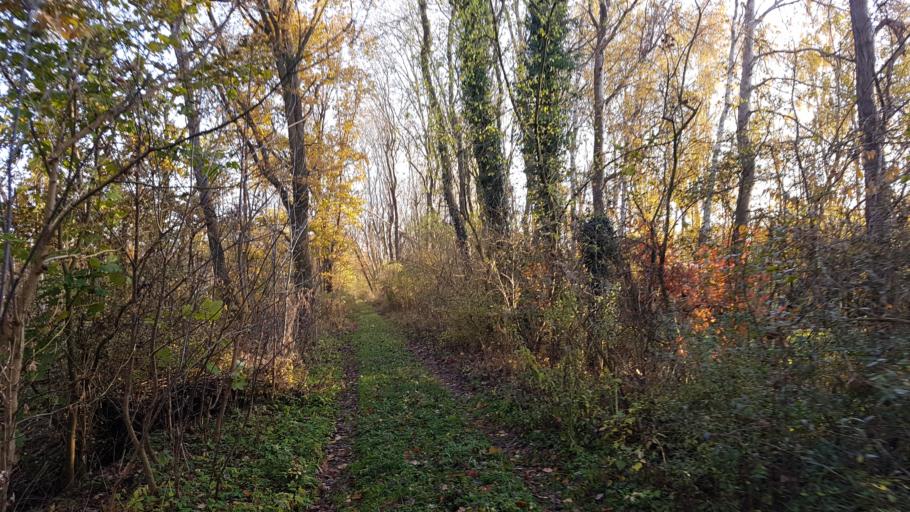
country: DE
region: Brandenburg
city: Trobitz
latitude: 51.5844
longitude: 13.4092
